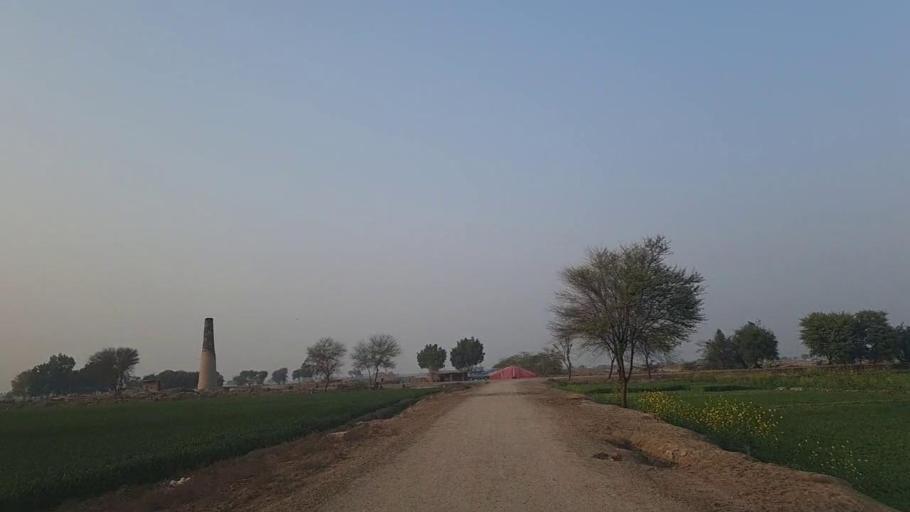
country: PK
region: Sindh
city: Nawabshah
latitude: 26.2560
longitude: 68.4712
